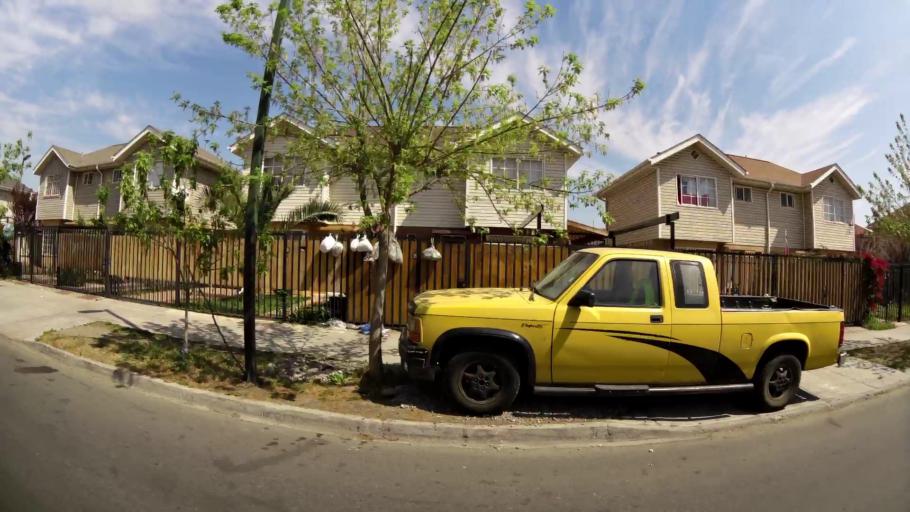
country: CL
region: Santiago Metropolitan
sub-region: Provincia de Cordillera
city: Puente Alto
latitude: -33.5939
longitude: -70.5905
